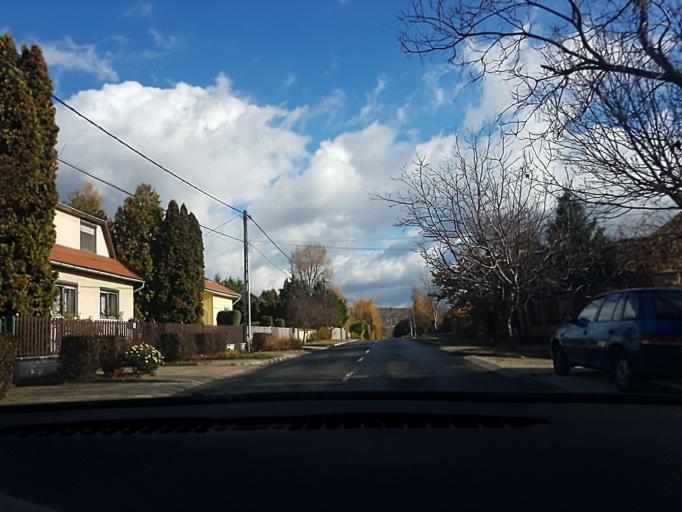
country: HU
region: Pest
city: Godollo
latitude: 47.6122
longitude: 19.3402
